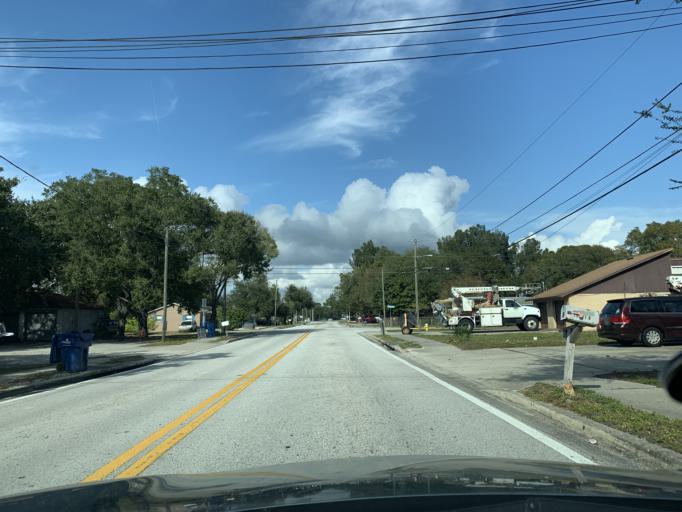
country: US
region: Florida
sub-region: Pinellas County
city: South Highpoint
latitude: 27.9137
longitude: -82.7133
